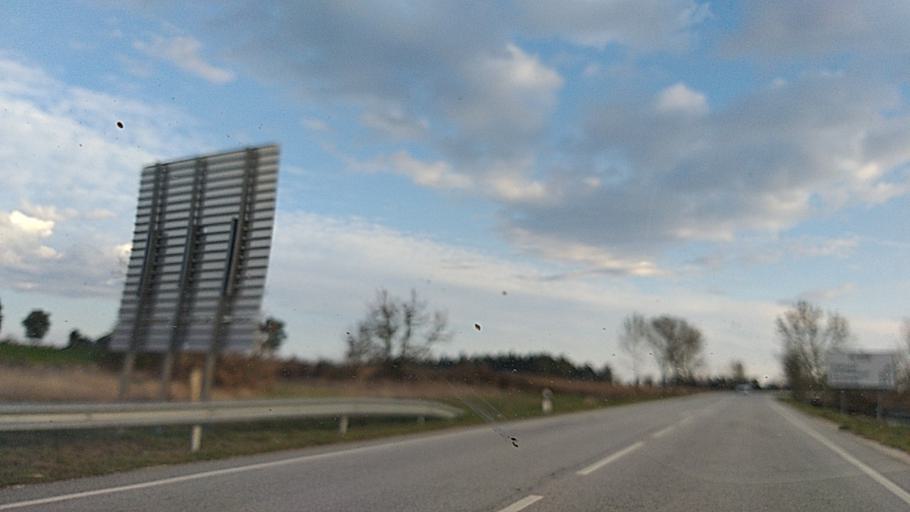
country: PT
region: Guarda
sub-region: Pinhel
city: Pinhel
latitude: 40.6591
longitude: -6.9676
